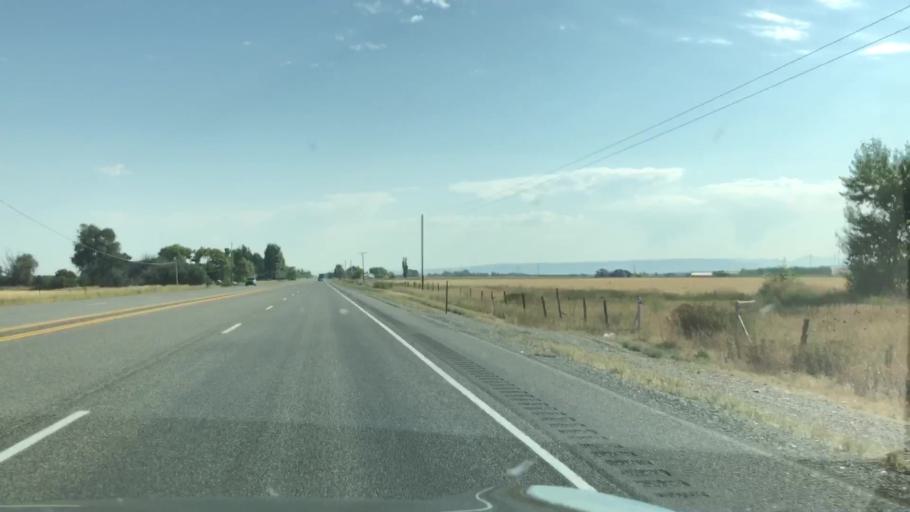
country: US
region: Idaho
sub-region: Bonneville County
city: Iona
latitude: 43.5706
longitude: -111.9139
